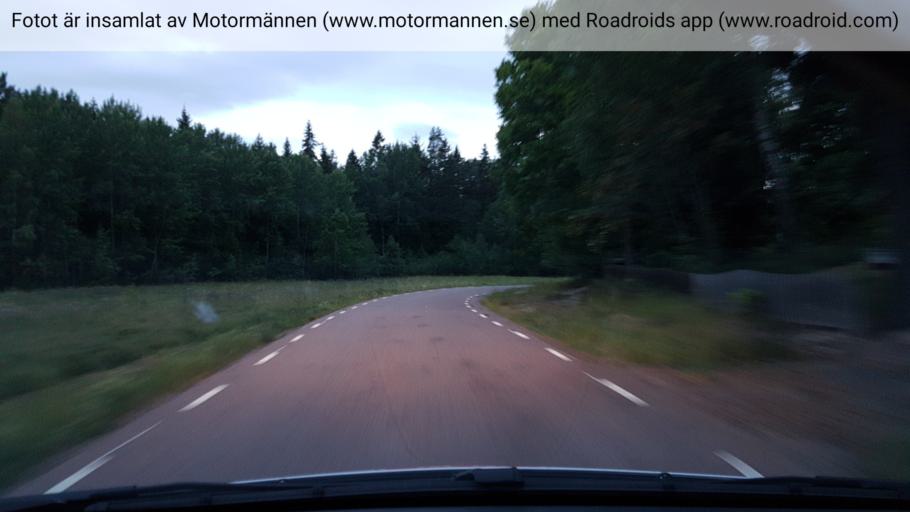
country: SE
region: Vaestmanland
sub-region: Vasteras
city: Tillberga
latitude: 59.5337
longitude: 16.7279
